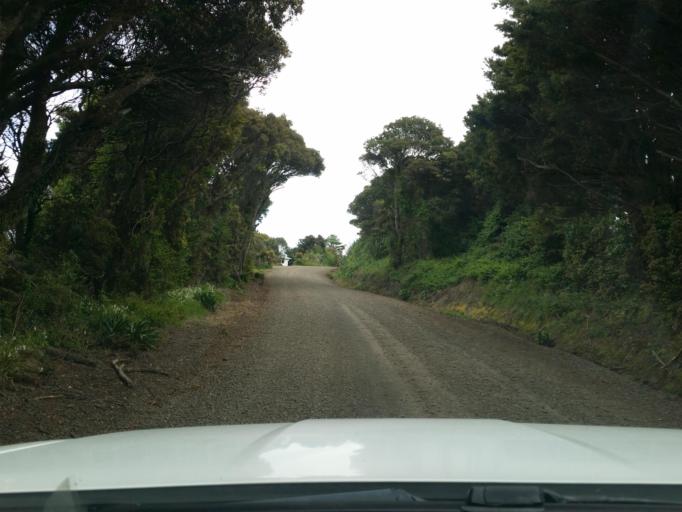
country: NZ
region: Northland
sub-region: Kaipara District
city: Dargaville
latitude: -35.7326
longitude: 173.6013
